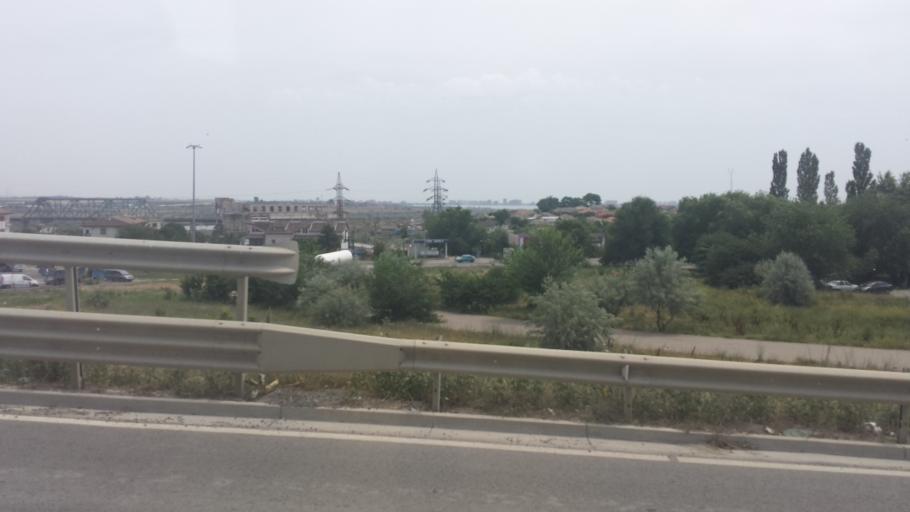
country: RO
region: Constanta
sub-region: Comuna Ovidiu
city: Ovidiu
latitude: 44.2616
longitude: 28.5533
